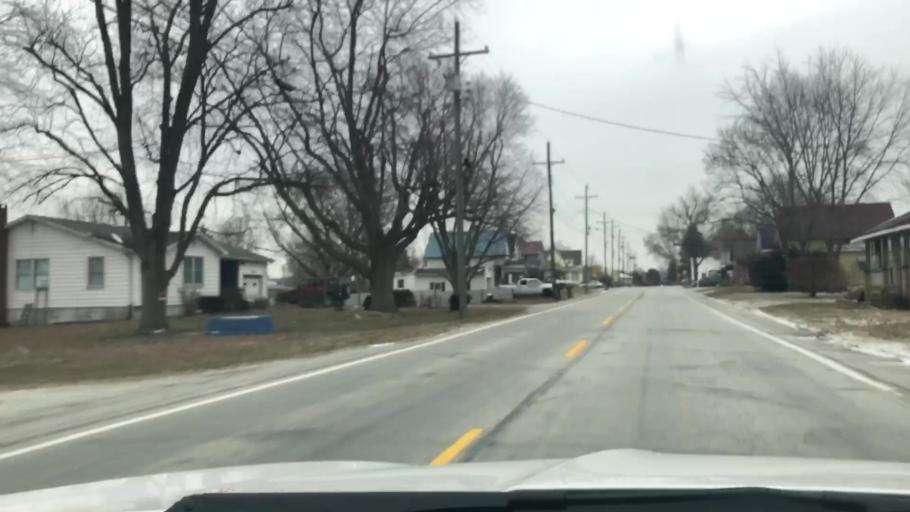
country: US
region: Indiana
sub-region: Fulton County
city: Rochester
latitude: 41.0542
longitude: -86.1278
